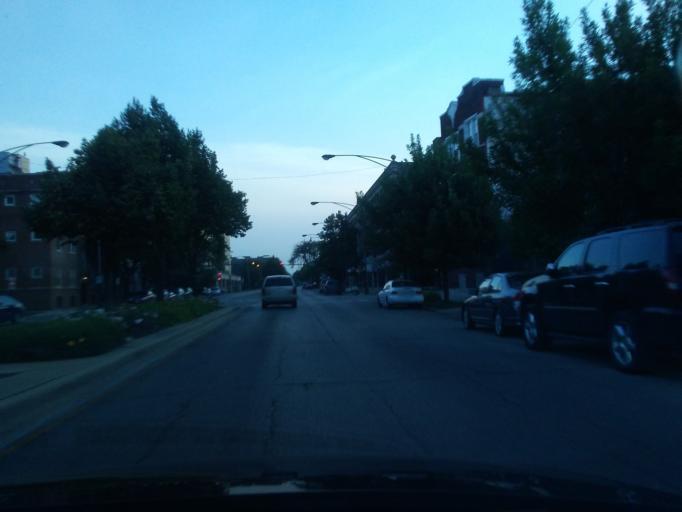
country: US
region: Illinois
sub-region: Cook County
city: Evanston
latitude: 41.9839
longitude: -87.6698
